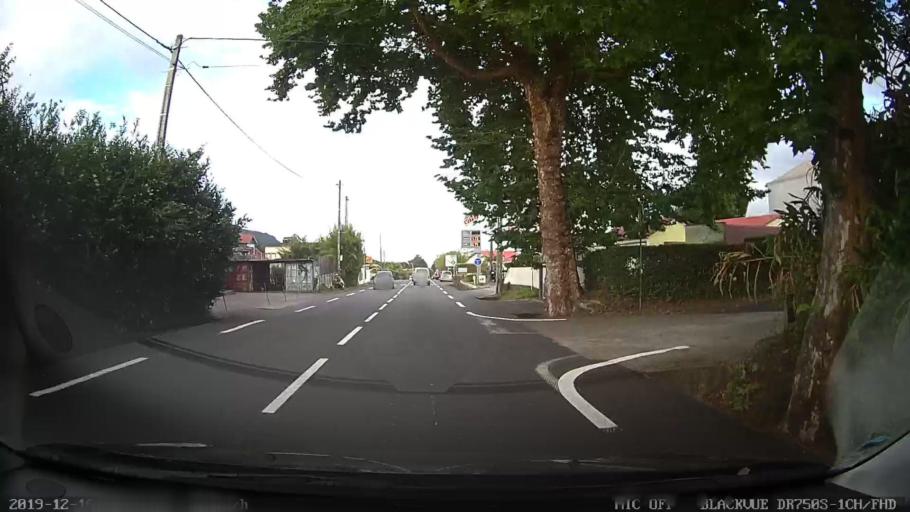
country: RE
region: Reunion
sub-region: Reunion
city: Salazie
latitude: -21.1451
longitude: 55.6188
